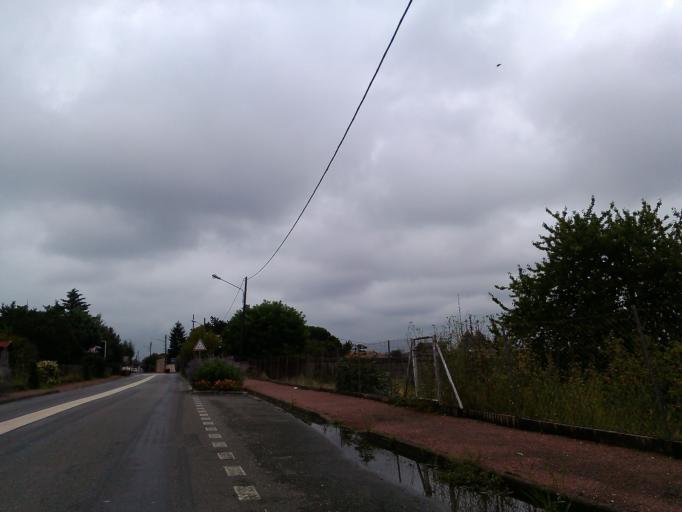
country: FR
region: Poitou-Charentes
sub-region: Departement de la Charente
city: Cognac
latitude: 45.6961
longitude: -0.3452
